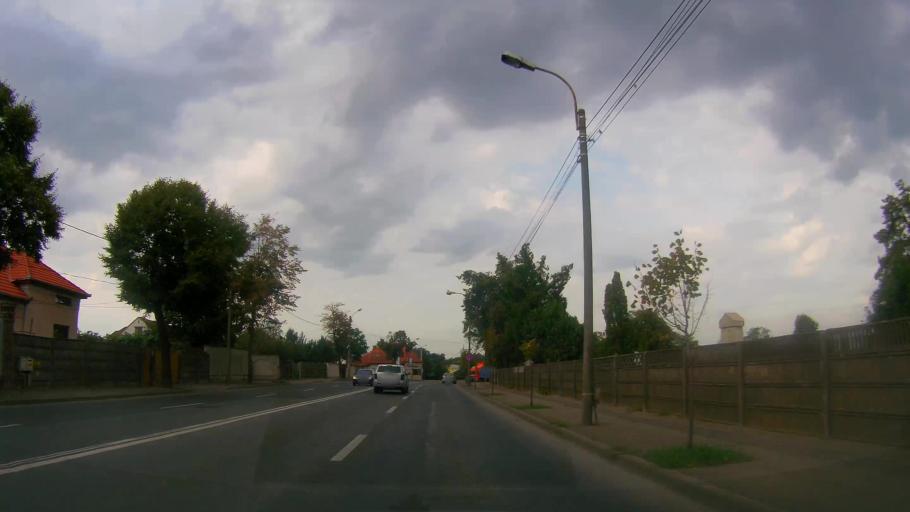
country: RO
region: Satu Mare
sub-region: Municipiul Satu Mare
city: Satu Mare
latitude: 47.7907
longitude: 22.8911
